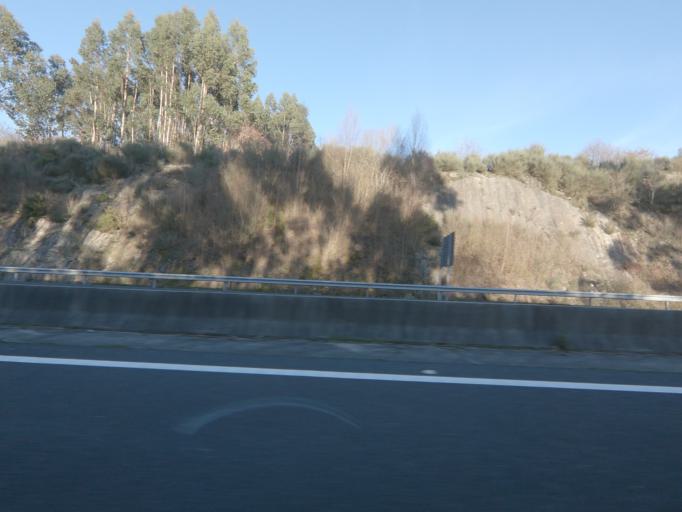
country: ES
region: Galicia
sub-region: Provincia de Ourense
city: Pinor
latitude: 42.4923
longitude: -8.0250
